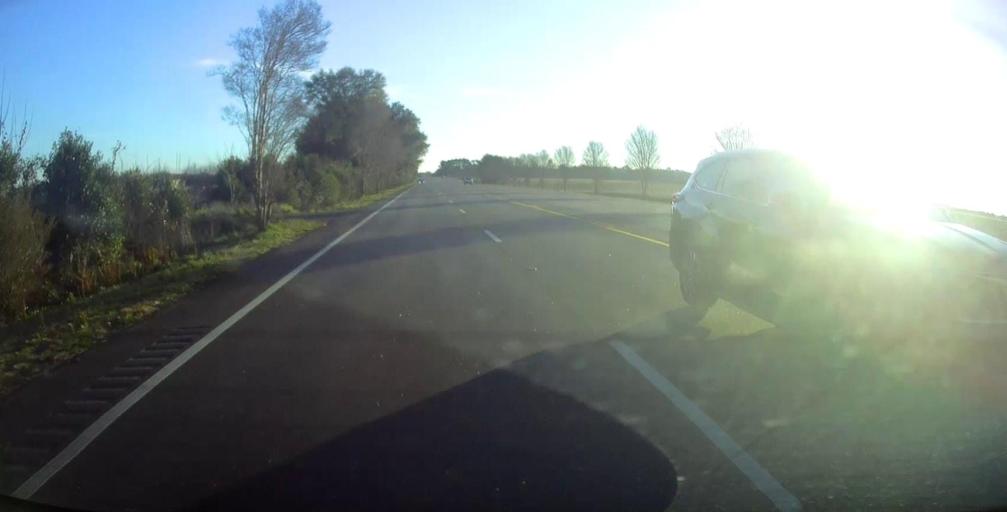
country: US
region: Georgia
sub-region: Dougherty County
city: Albany
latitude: 31.5276
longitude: -84.1905
